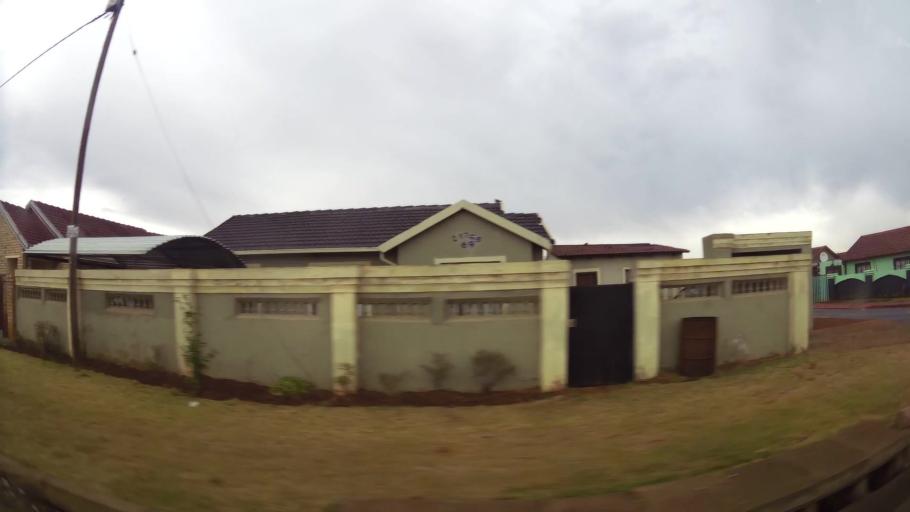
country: ZA
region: Gauteng
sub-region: Ekurhuleni Metropolitan Municipality
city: Germiston
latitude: -26.3330
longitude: 28.2023
